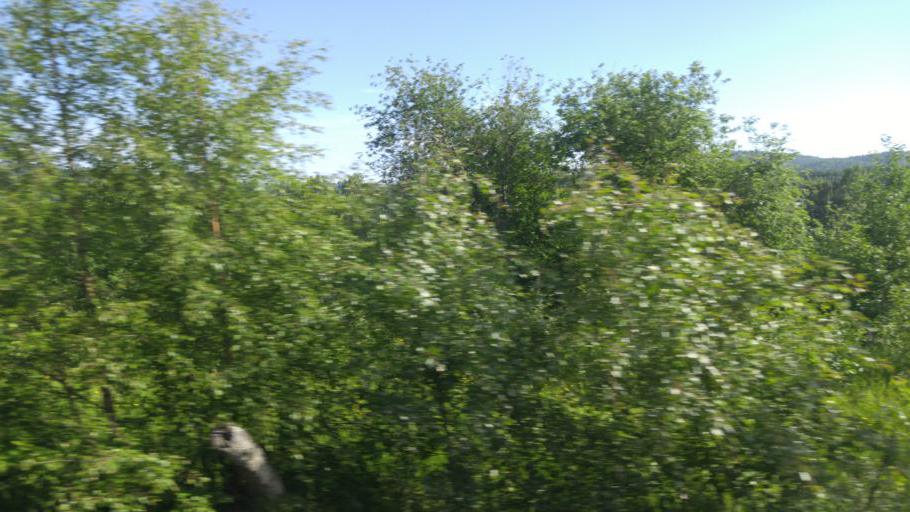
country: NO
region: Nord-Trondelag
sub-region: Stjordal
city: Stjordalshalsen
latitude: 63.4609
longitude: 11.1103
